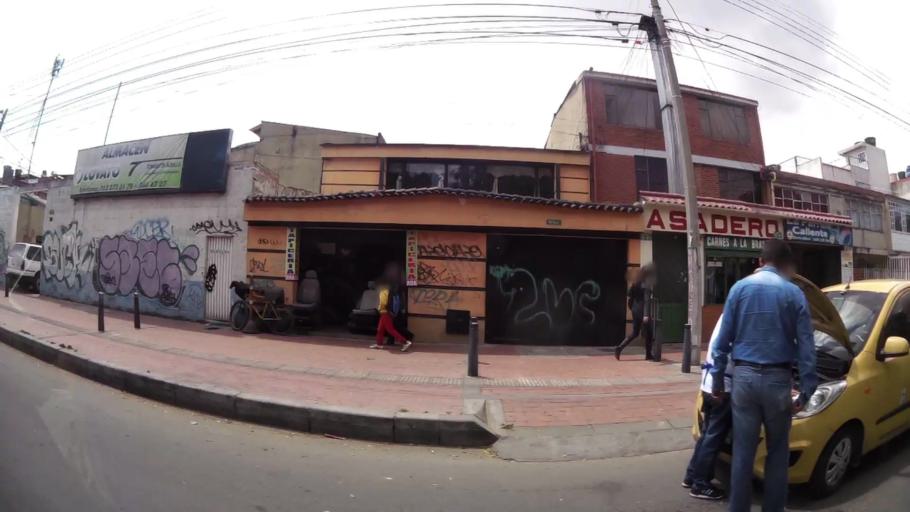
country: CO
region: Bogota D.C.
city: Bogota
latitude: 4.5802
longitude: -74.0993
